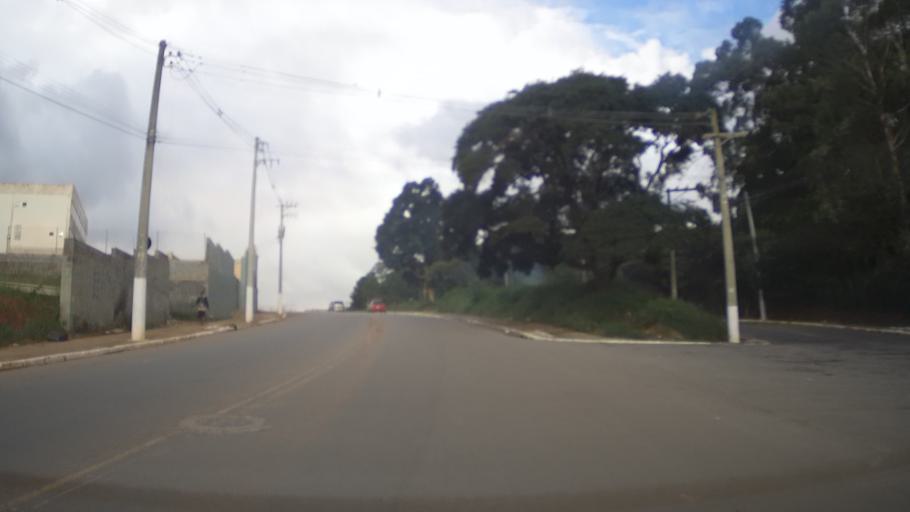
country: BR
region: Sao Paulo
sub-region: Itaquaquecetuba
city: Itaquaquecetuba
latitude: -23.4542
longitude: -46.4275
